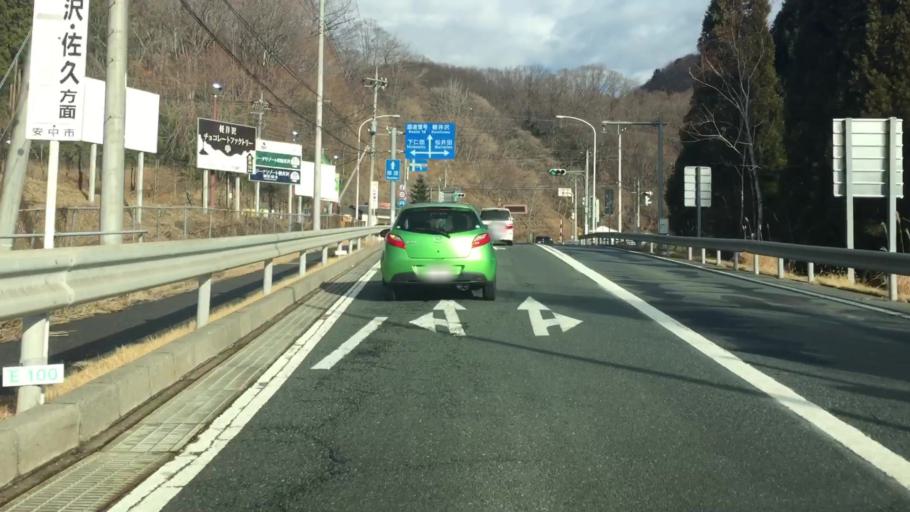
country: JP
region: Nagano
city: Saku
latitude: 36.2984
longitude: 138.6702
